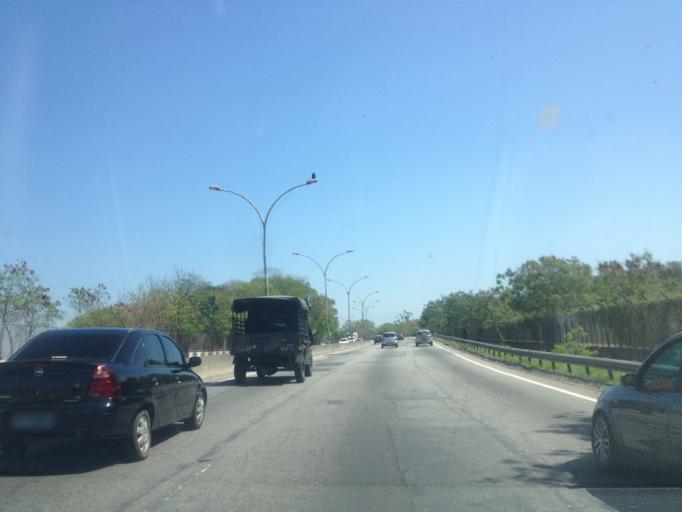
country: BR
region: Rio de Janeiro
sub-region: Duque De Caxias
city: Duque de Caxias
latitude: -22.8207
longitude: -43.2563
